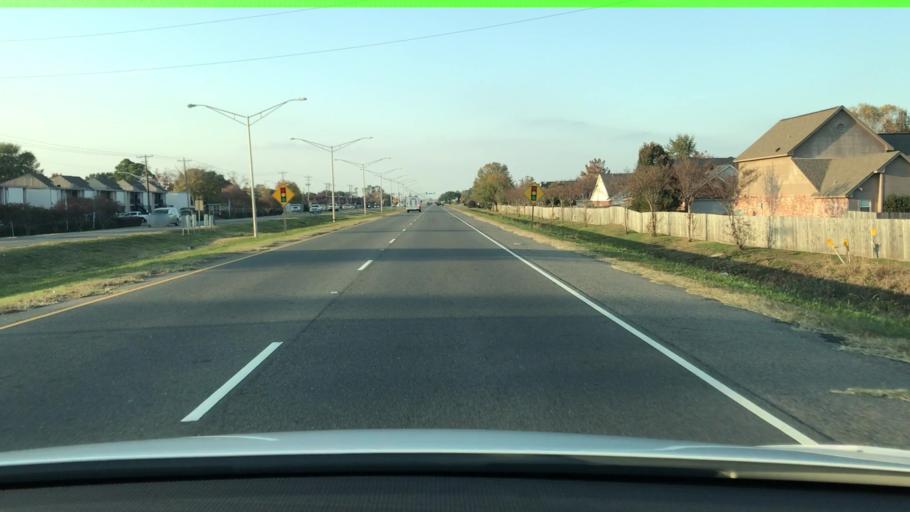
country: US
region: Louisiana
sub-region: Bossier Parish
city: Bossier City
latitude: 32.4098
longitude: -93.6990
